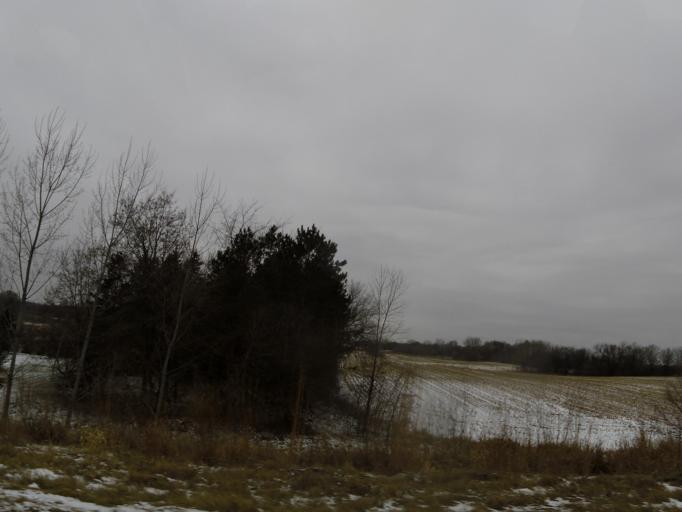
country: US
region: Minnesota
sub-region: Wright County
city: Montrose
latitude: 45.0604
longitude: -93.8588
